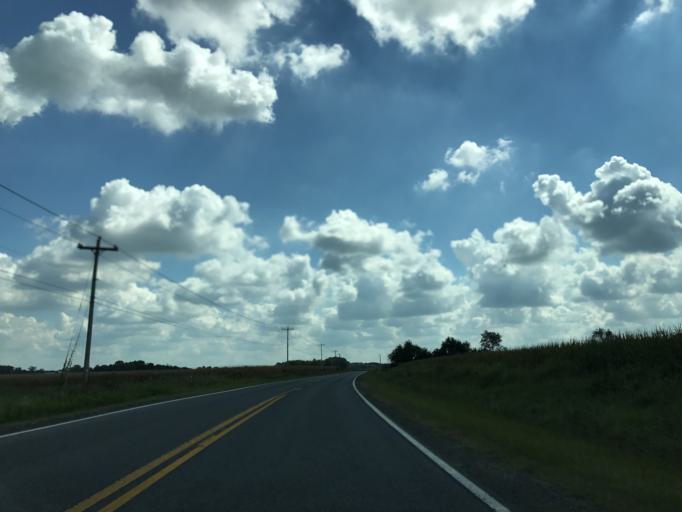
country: US
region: Maryland
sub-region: Queen Anne's County
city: Centreville
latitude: 39.0125
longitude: -75.9954
